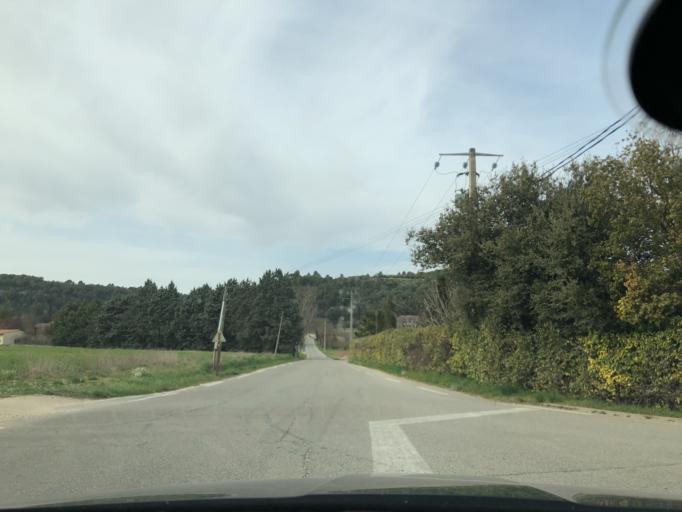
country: FR
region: Provence-Alpes-Cote d'Azur
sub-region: Departement du Vaucluse
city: Goult
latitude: 43.8543
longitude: 5.2397
